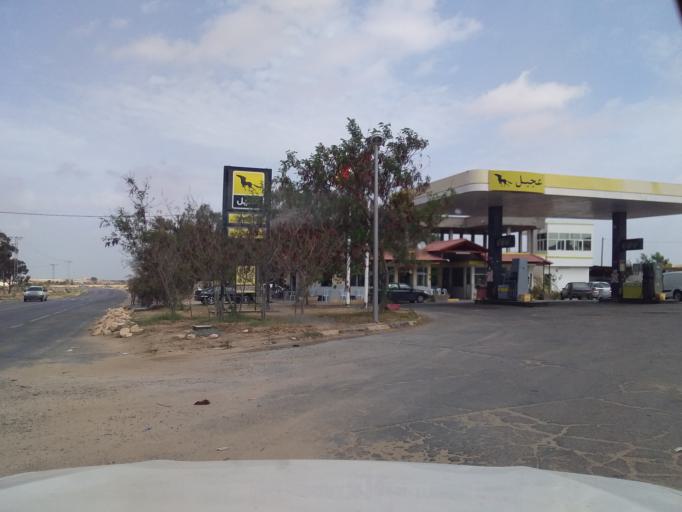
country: TN
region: Qabis
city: Gabes
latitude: 33.6373
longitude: 10.2826
